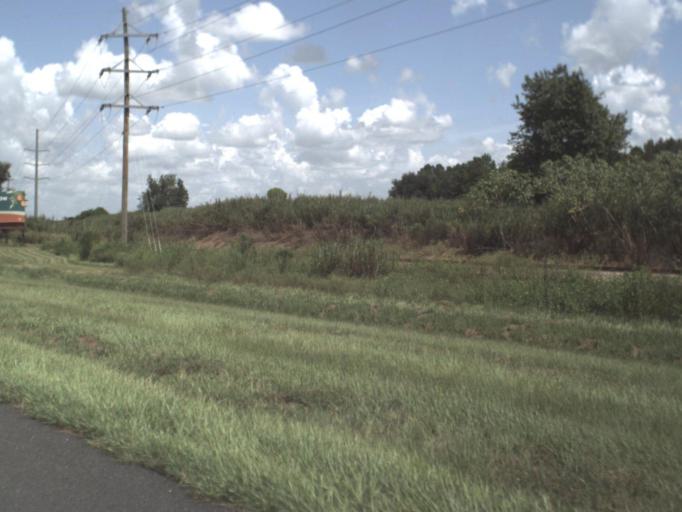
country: US
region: Florida
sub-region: Polk County
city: Bartow
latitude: 27.8523
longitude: -81.8264
